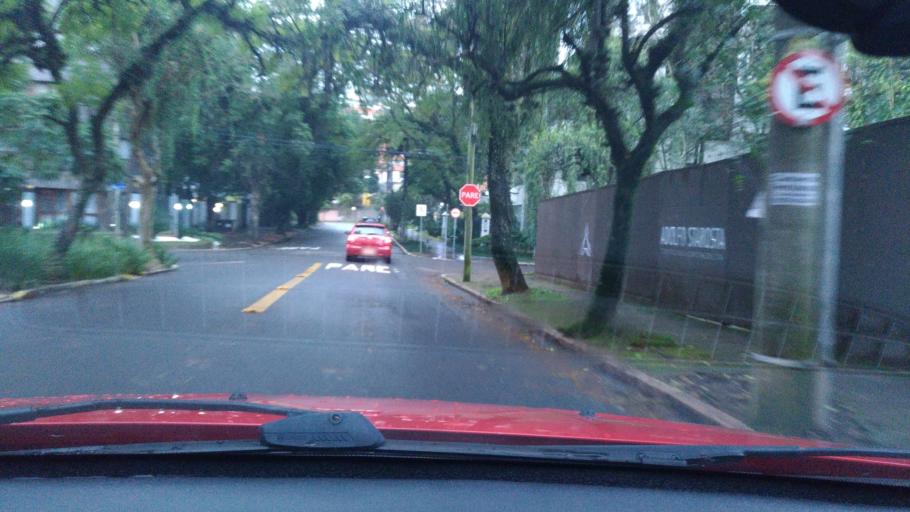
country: BR
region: Rio Grande do Sul
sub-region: Porto Alegre
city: Porto Alegre
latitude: -30.0280
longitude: -51.1865
